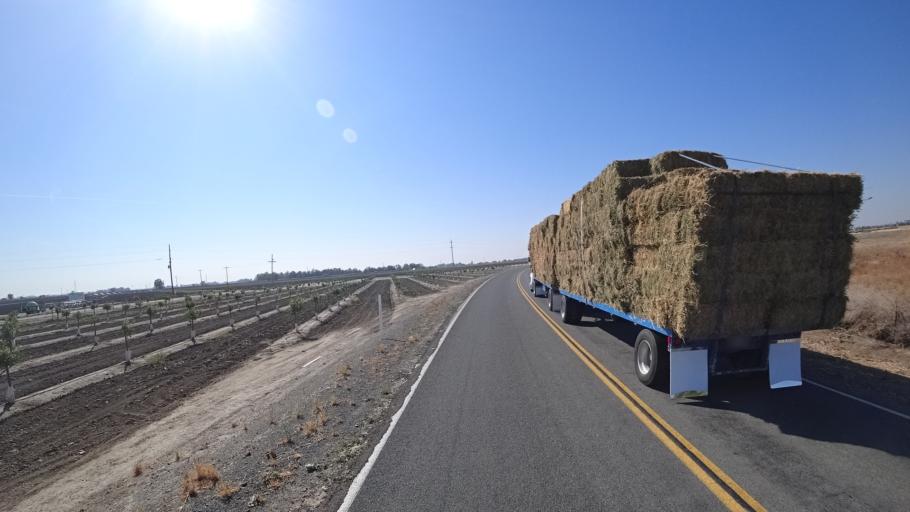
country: US
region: California
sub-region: Fresno County
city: Riverdale
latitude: 36.3577
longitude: -119.9062
